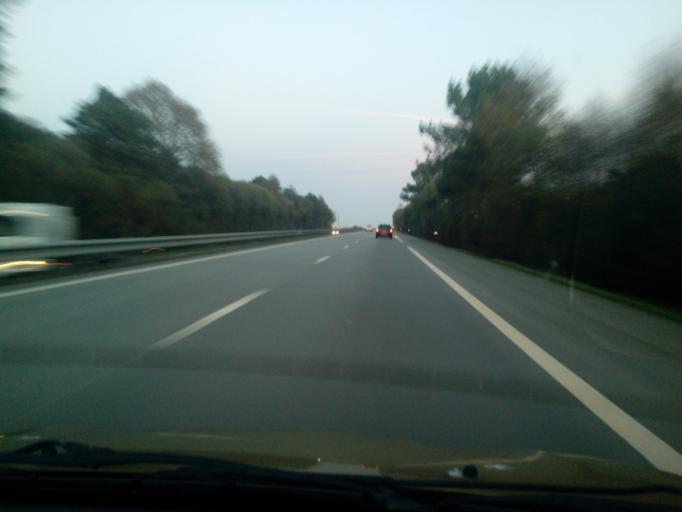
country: FR
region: Brittany
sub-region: Departement du Morbihan
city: Pleugriffet
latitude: 47.9219
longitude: -2.7030
